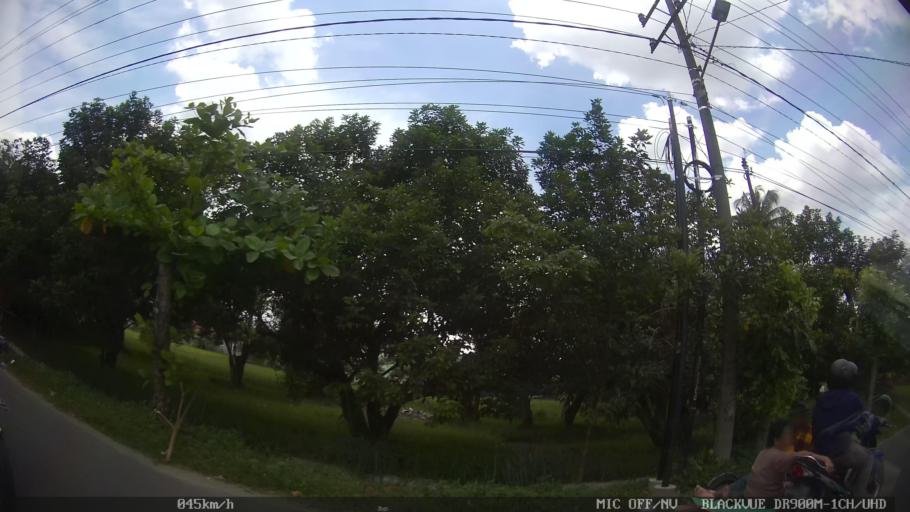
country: ID
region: North Sumatra
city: Binjai
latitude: 3.6279
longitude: 98.5108
